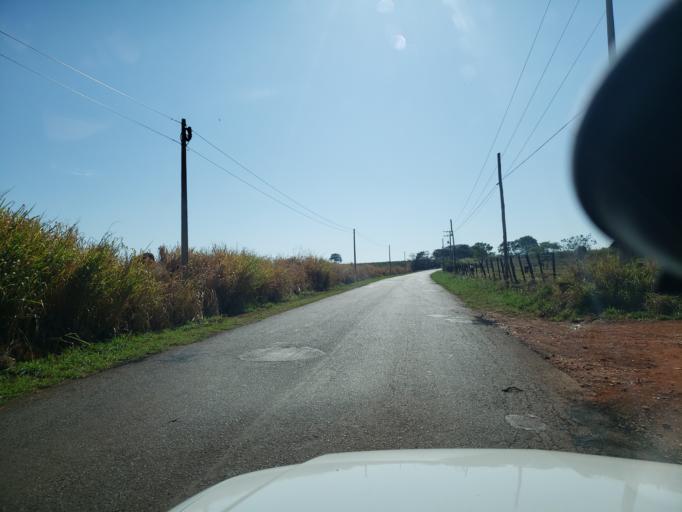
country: BR
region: Sao Paulo
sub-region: Moji-Guacu
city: Mogi-Gaucu
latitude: -22.3454
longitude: -46.8918
